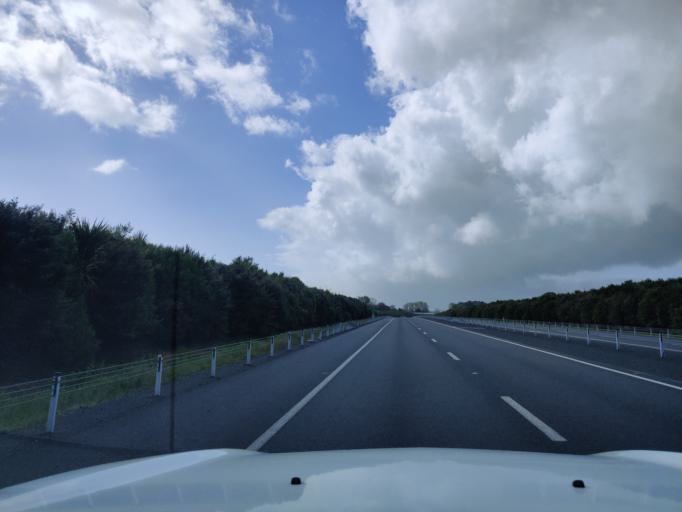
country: NZ
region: Waikato
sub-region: Waipa District
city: Cambridge
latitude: -37.8792
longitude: 175.4871
